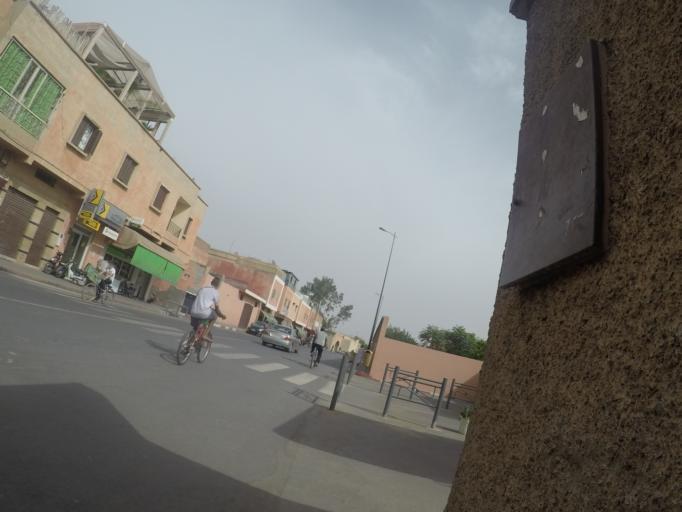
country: MA
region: Marrakech-Tensift-Al Haouz
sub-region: Marrakech
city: Marrakesh
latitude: 31.6245
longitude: -7.9761
